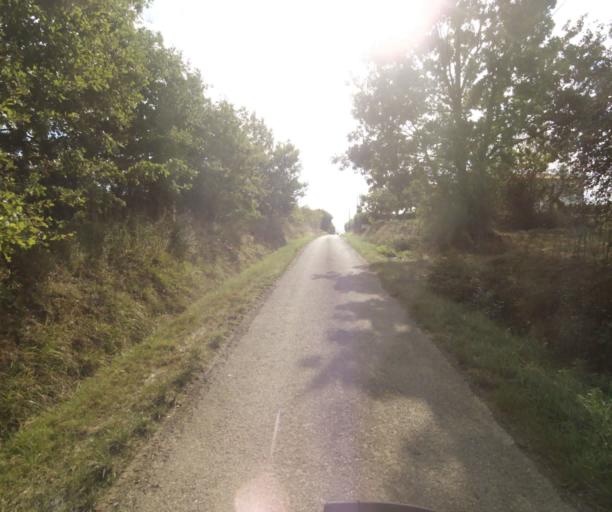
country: FR
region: Midi-Pyrenees
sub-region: Departement du Tarn-et-Garonne
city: Verdun-sur-Garonne
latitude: 43.8632
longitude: 1.1803
